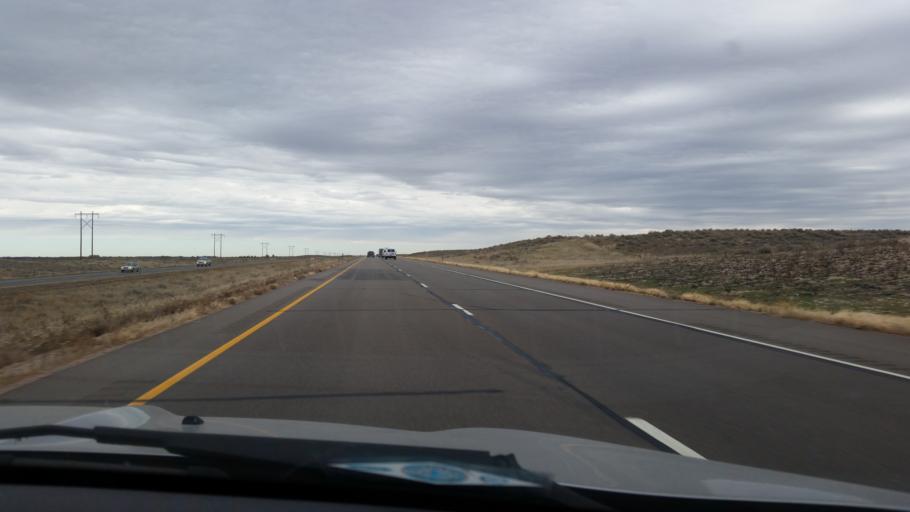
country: US
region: Colorado
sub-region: Morgan County
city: Brush
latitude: 40.3450
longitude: -103.4523
